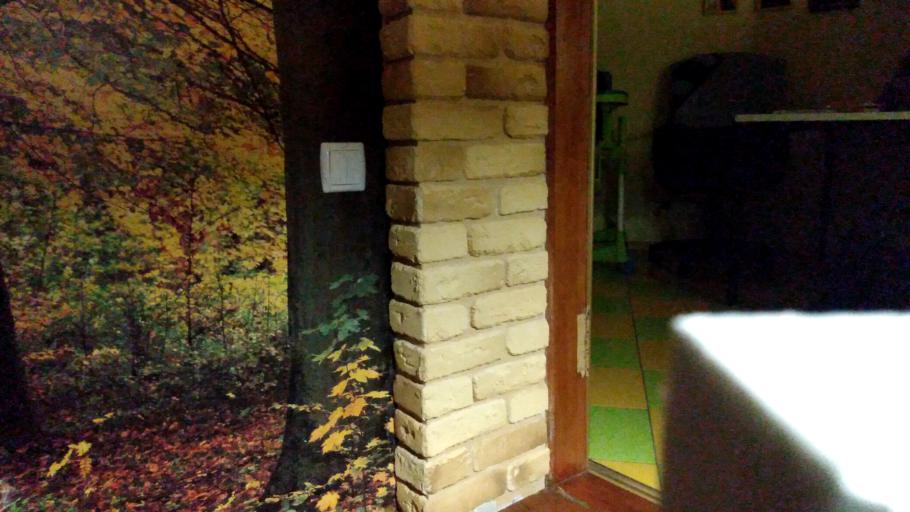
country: RU
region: Arkhangelskaya
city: Kargopol'
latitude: 61.4134
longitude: 37.8115
